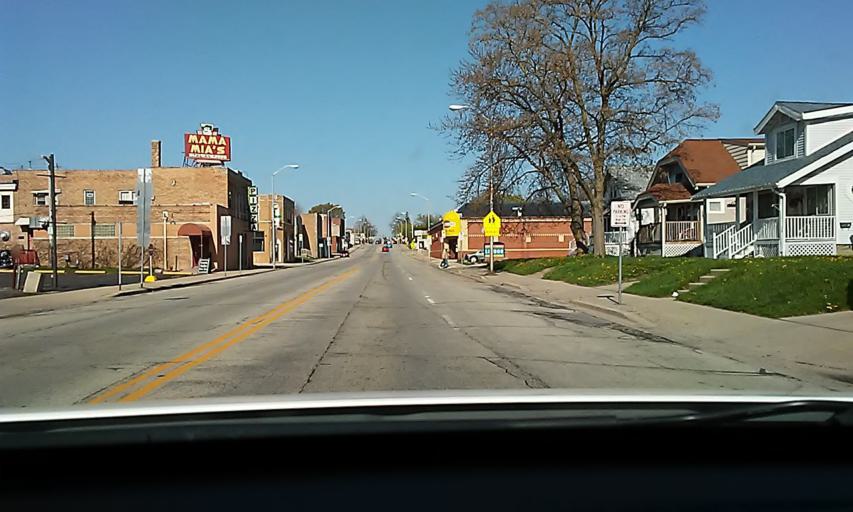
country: US
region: Wisconsin
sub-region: Milwaukee County
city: West Allis
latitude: 43.0166
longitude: -88.0187
